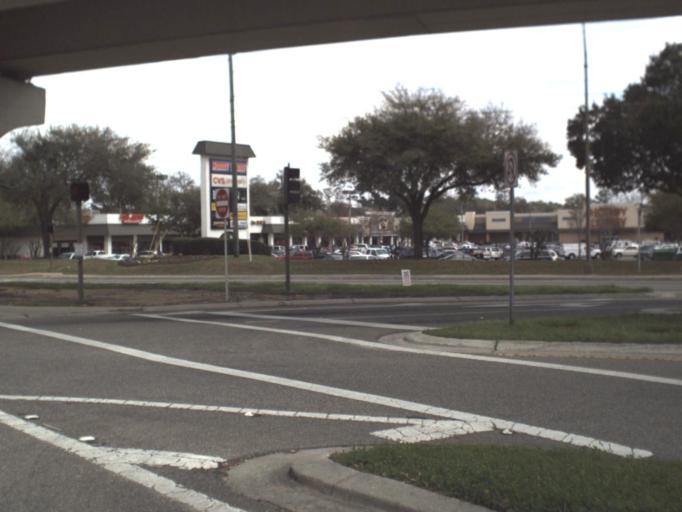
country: US
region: Florida
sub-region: Leon County
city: Tallahassee
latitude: 30.5063
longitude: -84.2500
